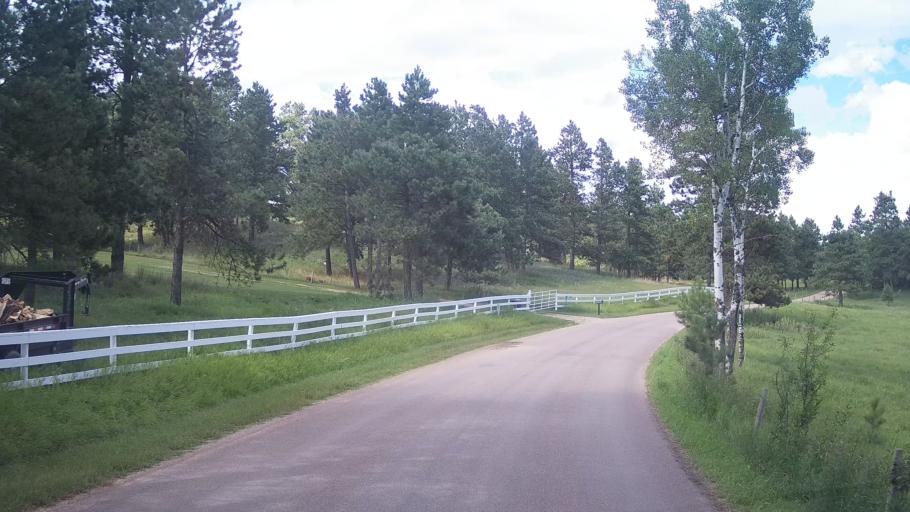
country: US
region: South Dakota
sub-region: Pennington County
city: Colonial Pine Hills
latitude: 43.8541
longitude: -103.3829
